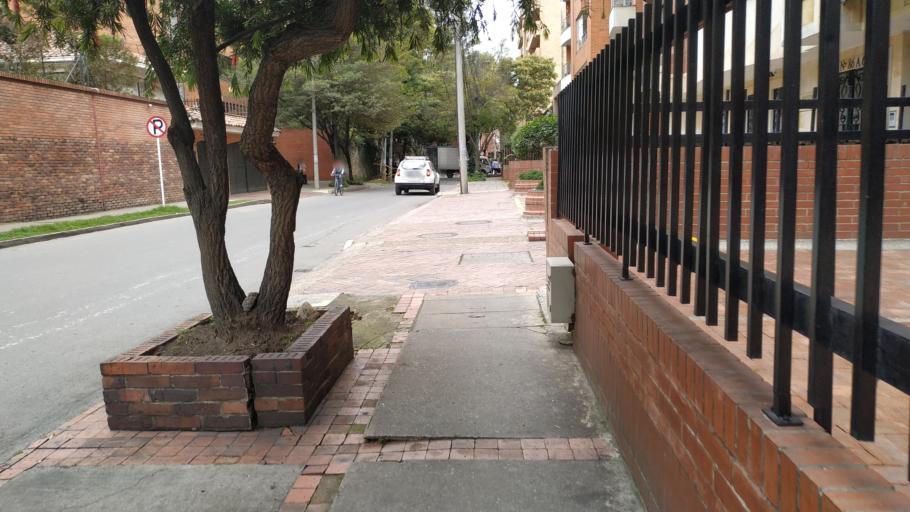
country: CO
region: Bogota D.C.
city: Barrio San Luis
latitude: 4.6715
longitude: -74.0524
